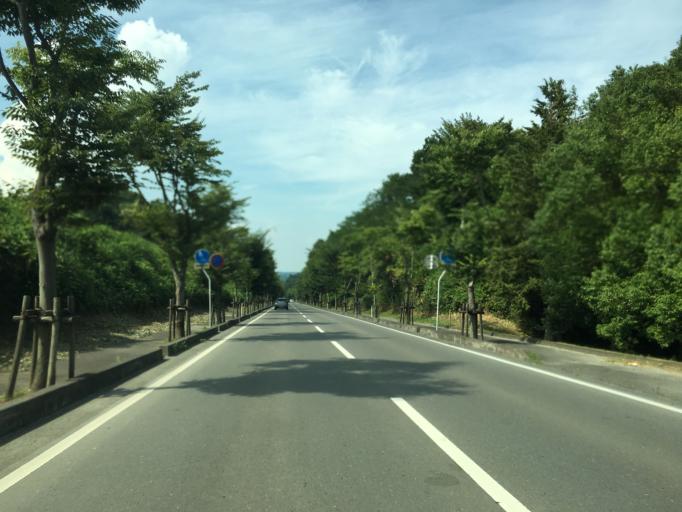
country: JP
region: Fukushima
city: Sukagawa
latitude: 37.2313
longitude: 140.4353
